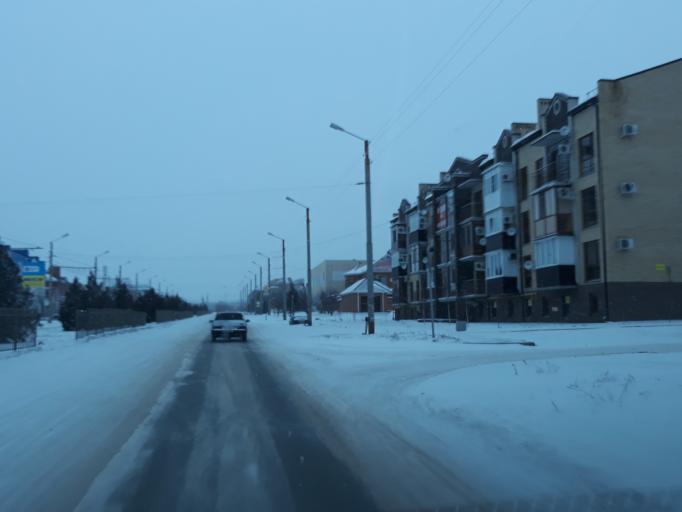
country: RU
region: Rostov
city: Taganrog
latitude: 47.2735
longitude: 38.9185
